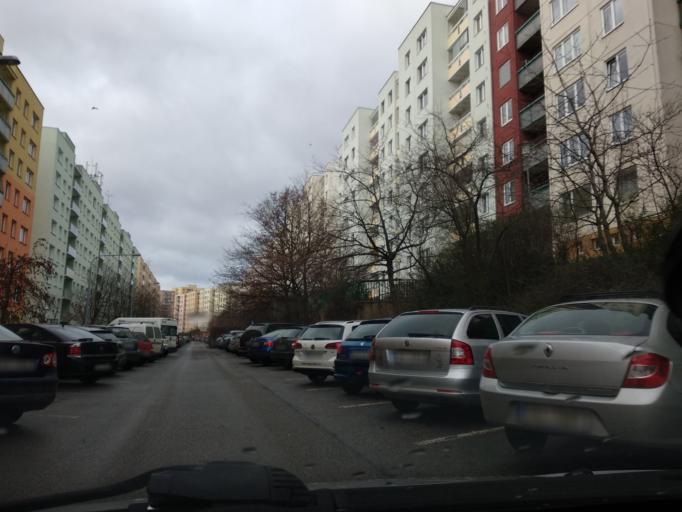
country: CZ
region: South Moravian
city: Ostopovice
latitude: 49.1759
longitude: 16.5576
